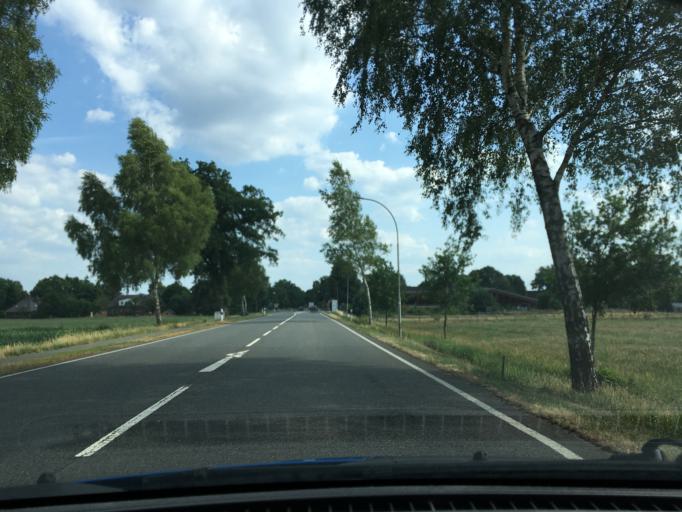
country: DE
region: Lower Saxony
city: Handeloh
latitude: 53.1872
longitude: 9.8341
